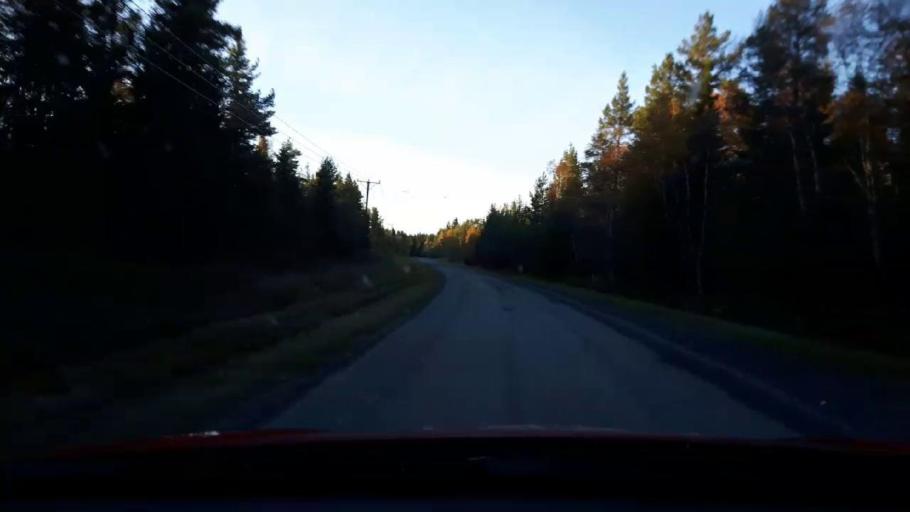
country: SE
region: Jaemtland
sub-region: Krokoms Kommun
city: Krokom
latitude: 63.4489
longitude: 14.4178
